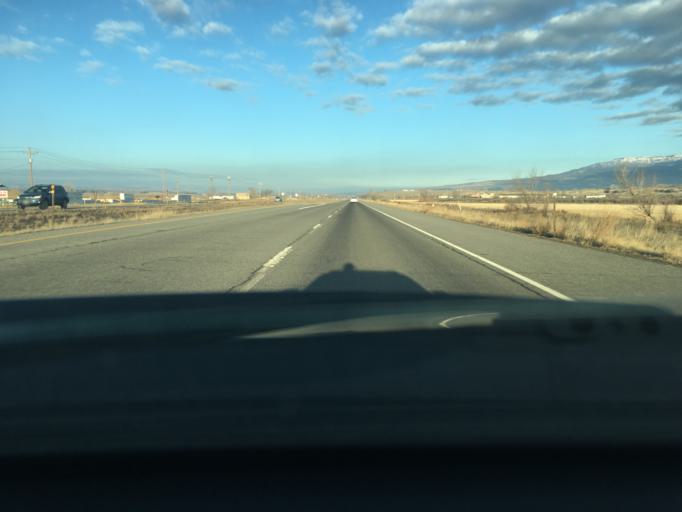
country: US
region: Colorado
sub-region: Delta County
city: Delta
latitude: 38.6967
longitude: -108.0242
